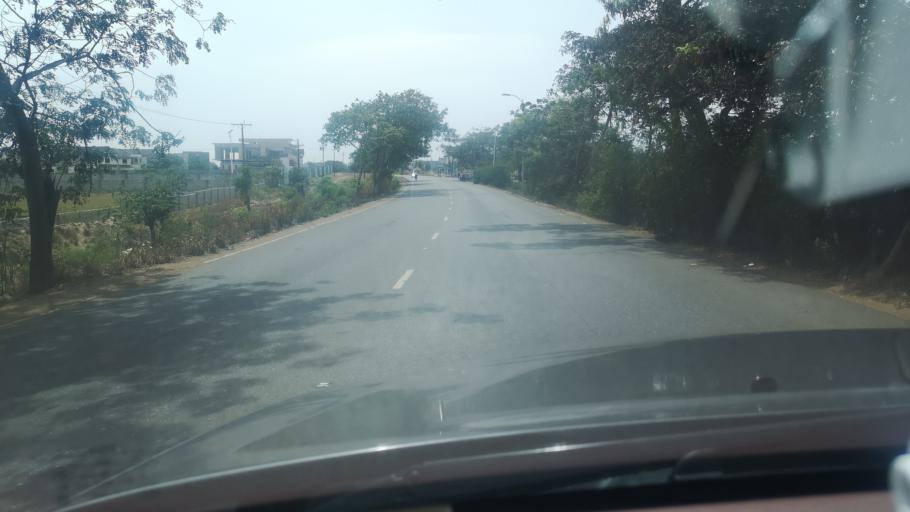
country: GH
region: Greater Accra
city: Nungua
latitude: 5.6154
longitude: -0.0602
